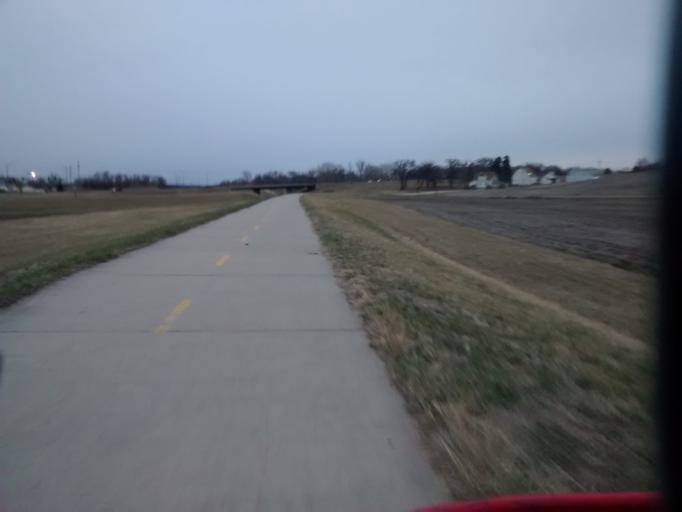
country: US
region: Nebraska
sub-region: Sarpy County
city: Offutt Air Force Base
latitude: 41.1461
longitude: -95.9644
